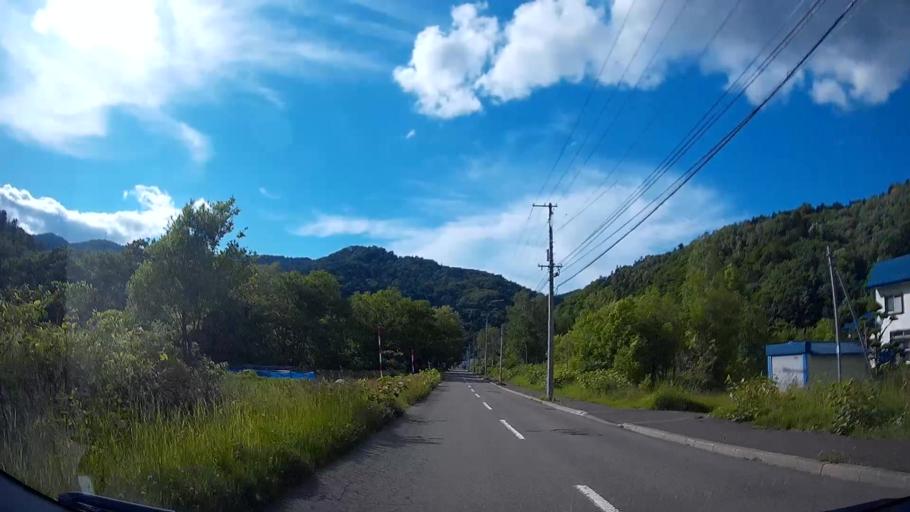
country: JP
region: Hokkaido
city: Sapporo
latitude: 42.9490
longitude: 141.1545
